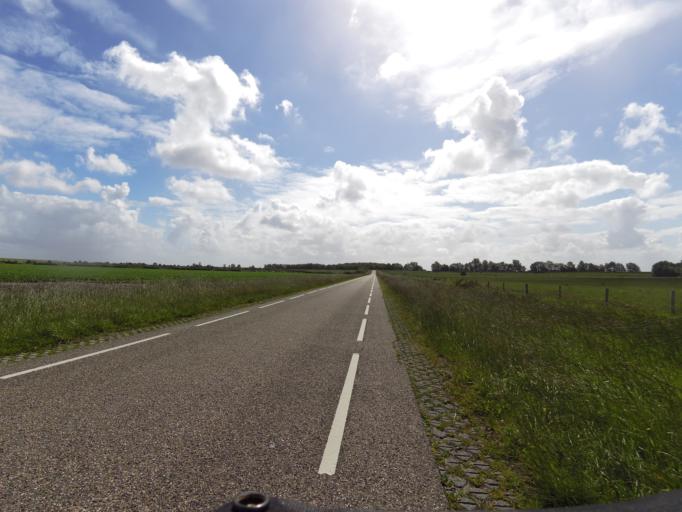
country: NL
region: Zeeland
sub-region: Schouwen-Duiveland
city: Bruinisse
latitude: 51.6791
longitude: 4.0189
